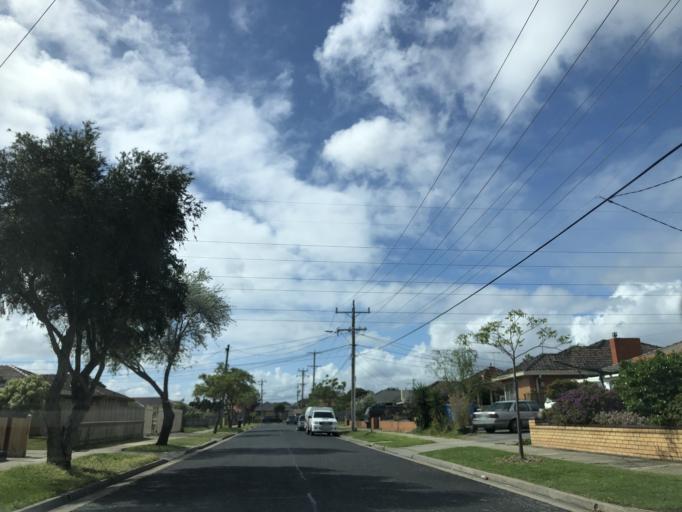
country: AU
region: Victoria
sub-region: Kingston
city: Clayton South
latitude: -37.9384
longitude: 145.1141
